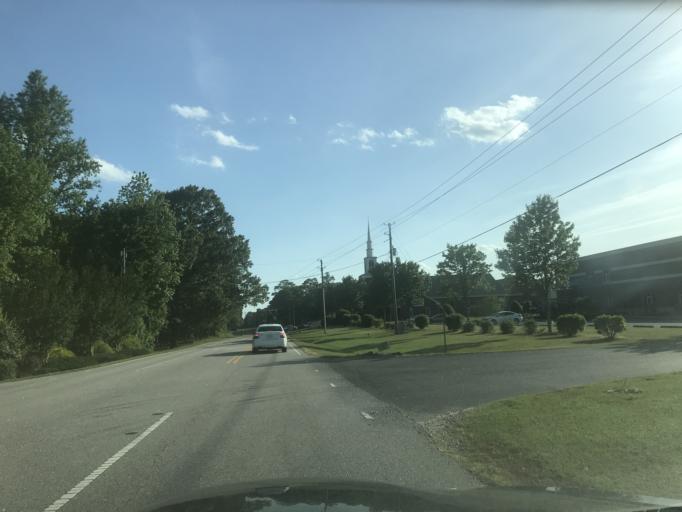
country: US
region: North Carolina
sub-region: Wake County
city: Wendell
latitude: 35.7684
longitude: -78.4078
